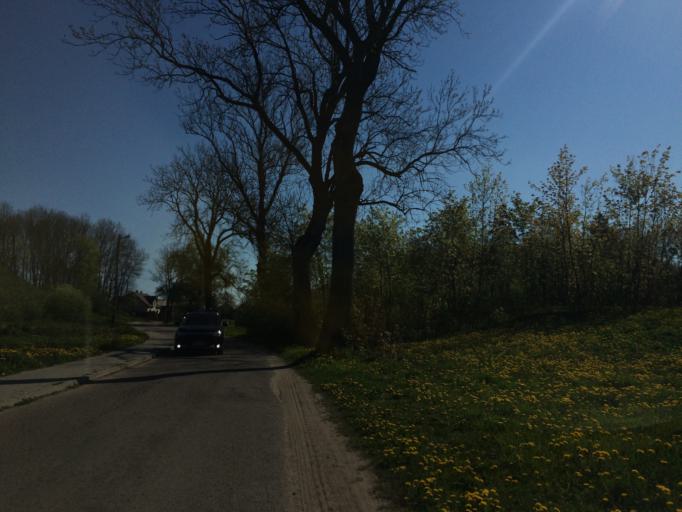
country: PL
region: Warmian-Masurian Voivodeship
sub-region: Powiat dzialdowski
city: Rybno
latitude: 53.4588
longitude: 19.9473
